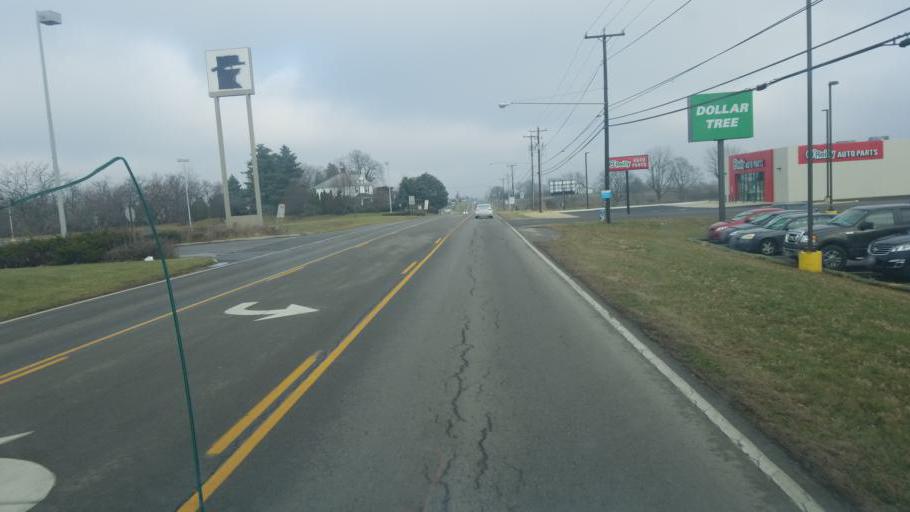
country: US
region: Ohio
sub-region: Hardin County
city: Kenton
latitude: 40.6526
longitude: -83.5896
